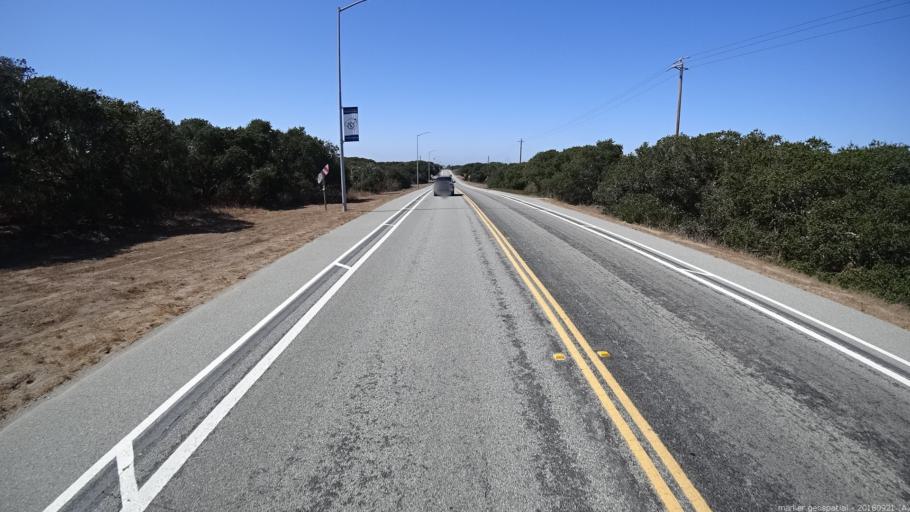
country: US
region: California
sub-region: Monterey County
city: Marina
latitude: 36.6552
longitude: -121.7710
